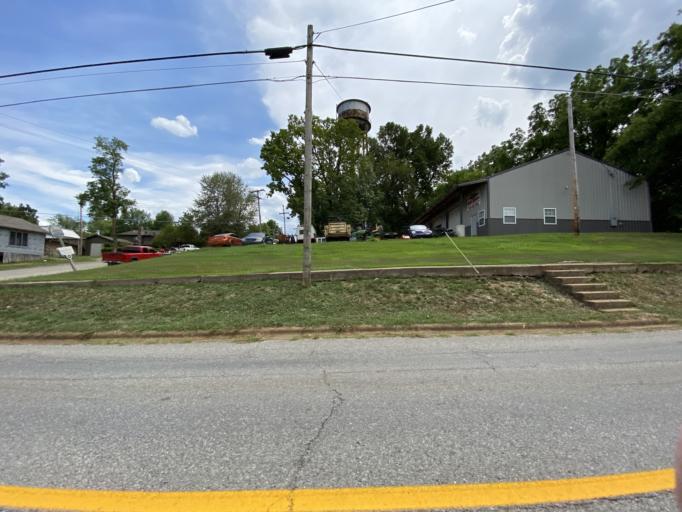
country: US
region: Missouri
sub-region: Oregon County
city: Thayer
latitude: 36.4957
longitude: -91.5431
